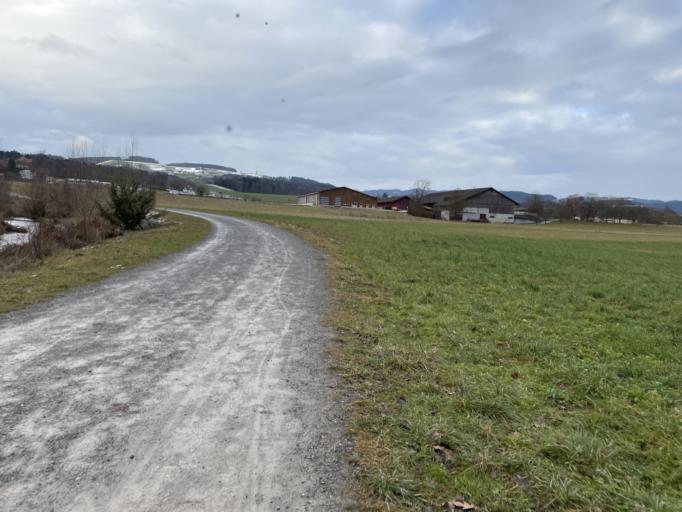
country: CH
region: Bern
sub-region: Bern-Mittelland District
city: Rubigen
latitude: 46.8853
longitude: 7.5462
